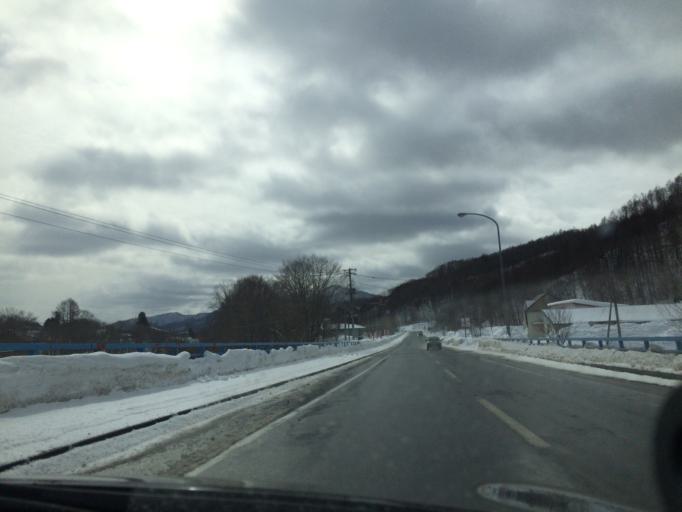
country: JP
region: Hokkaido
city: Iwamizawa
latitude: 43.0055
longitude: 142.0061
